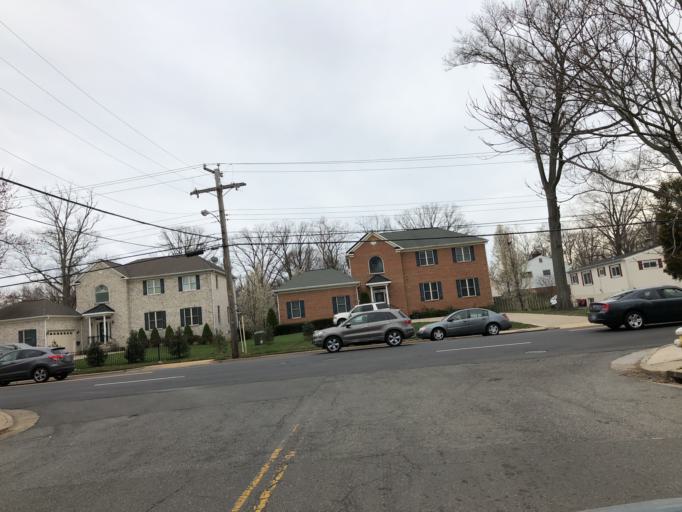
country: US
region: Virginia
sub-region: Fairfax County
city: Baileys Crossroads
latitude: 38.8385
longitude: -77.1199
